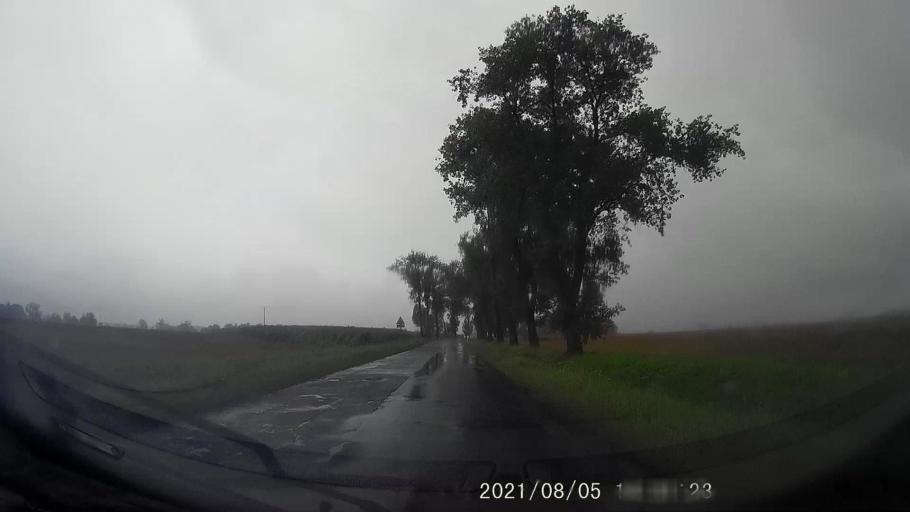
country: PL
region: Opole Voivodeship
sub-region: Powiat nyski
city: Korfantow
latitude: 50.4757
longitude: 17.5575
